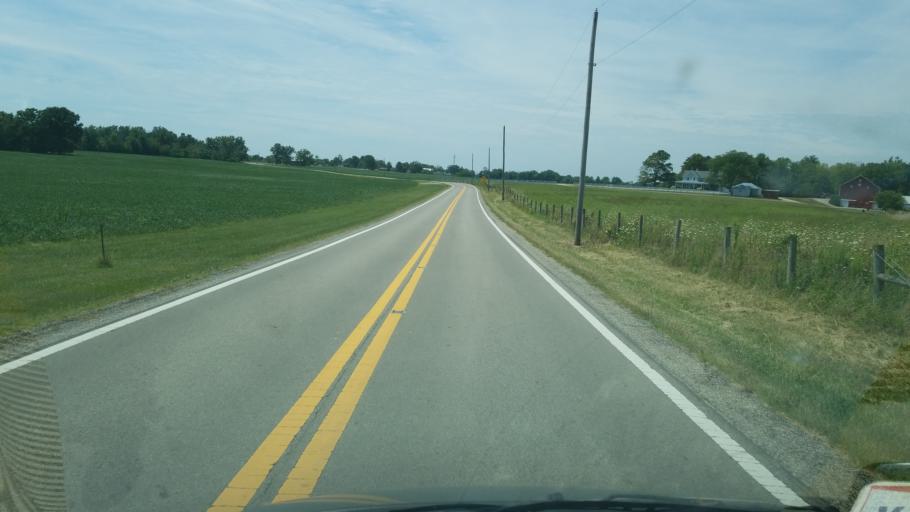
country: US
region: Ohio
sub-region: Madison County
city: Mount Sterling
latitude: 39.8284
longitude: -83.2198
